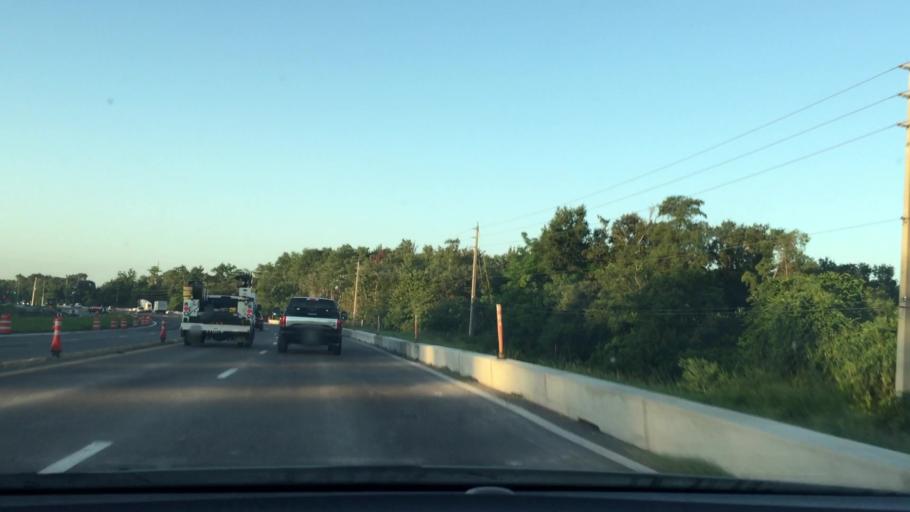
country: US
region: Florida
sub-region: Orange County
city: Fairview Shores
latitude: 28.5640
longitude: -81.4162
